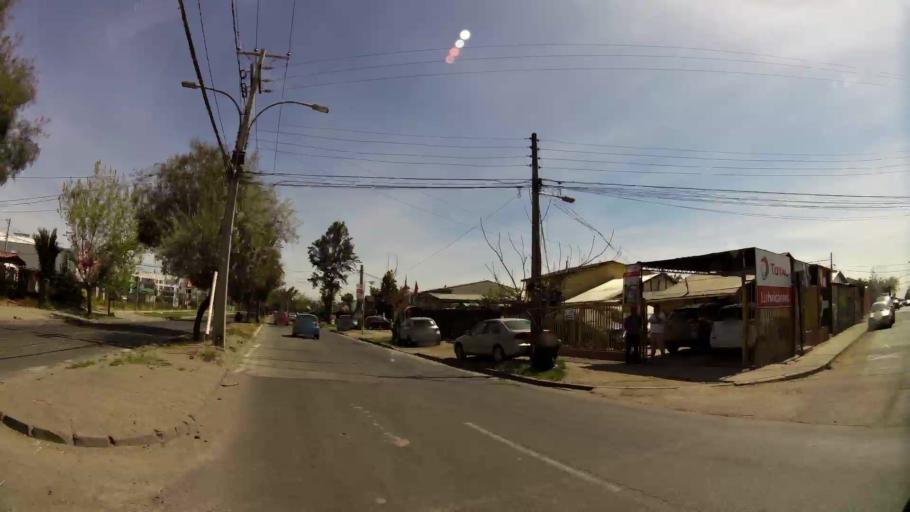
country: CL
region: Santiago Metropolitan
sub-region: Provincia de Cordillera
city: Puente Alto
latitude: -33.5769
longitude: -70.5731
